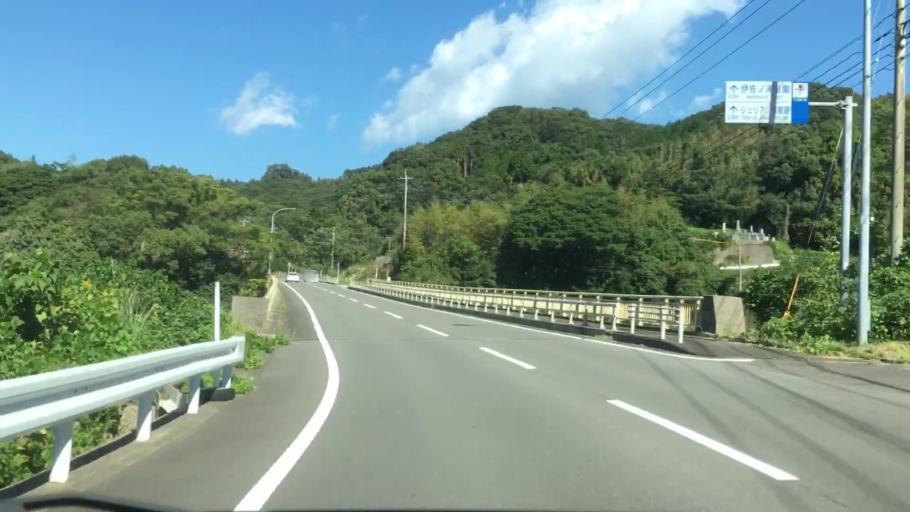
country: JP
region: Nagasaki
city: Sasebo
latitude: 33.0005
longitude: 129.6619
